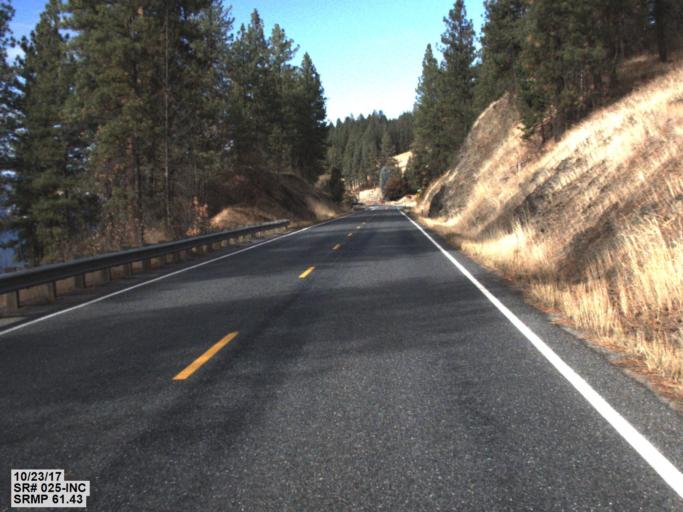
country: US
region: Washington
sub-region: Stevens County
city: Kettle Falls
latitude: 48.3586
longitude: -118.1631
